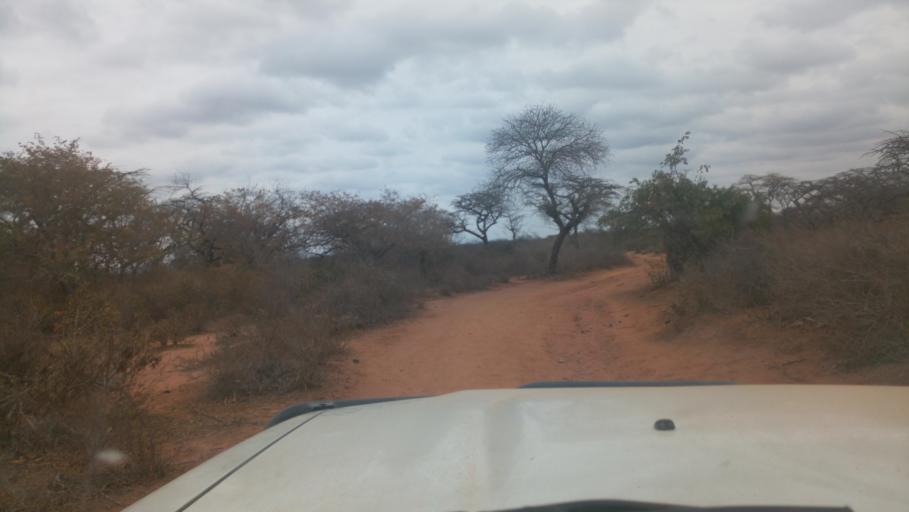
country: KE
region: Makueni
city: Wote
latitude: -1.9143
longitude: 38.0347
